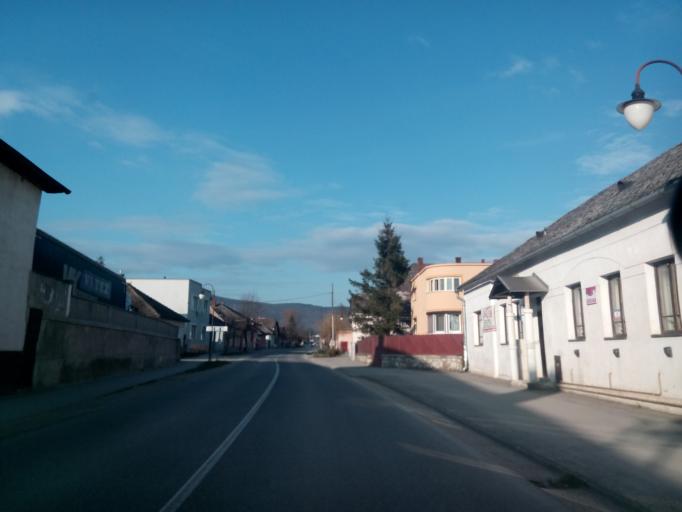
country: SK
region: Kosicky
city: Medzev
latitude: 48.5988
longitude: 20.8754
